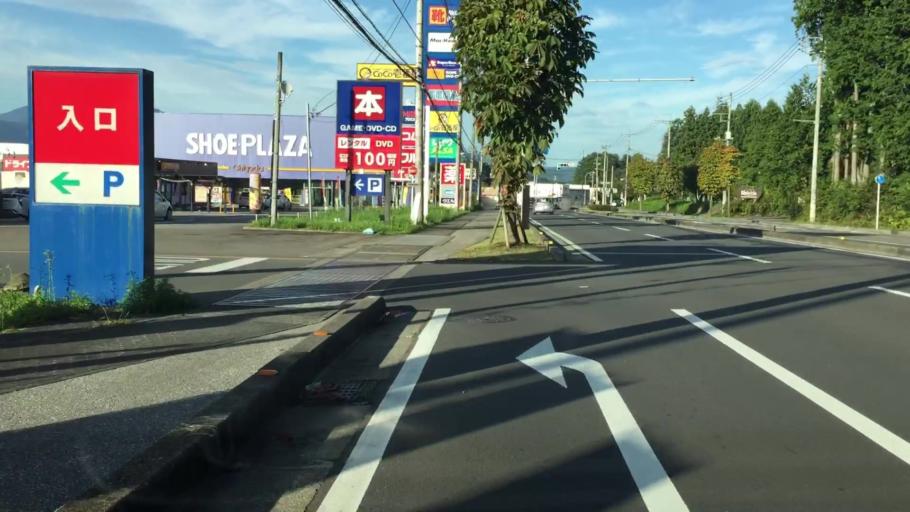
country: JP
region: Tochigi
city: Imaichi
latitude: 36.7410
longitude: 139.7110
